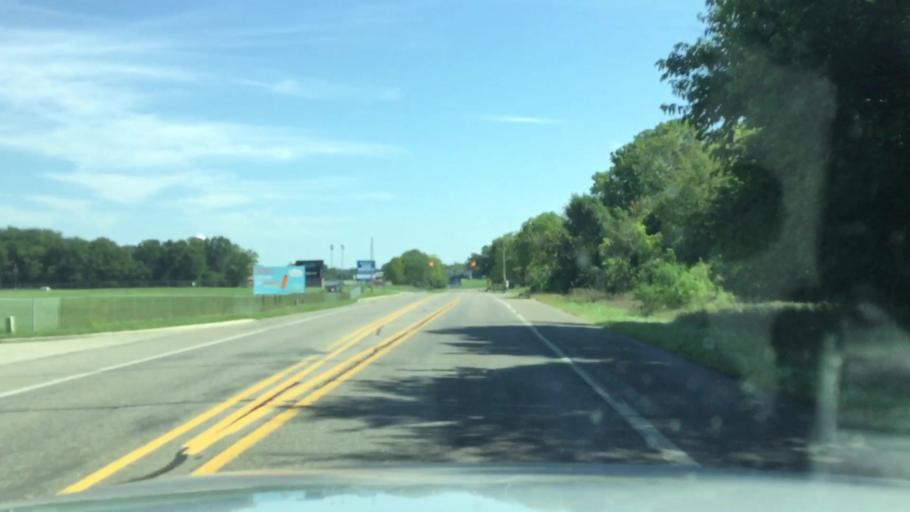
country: US
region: Michigan
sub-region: Jackson County
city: Brooklyn
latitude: 42.0576
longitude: -84.2494
